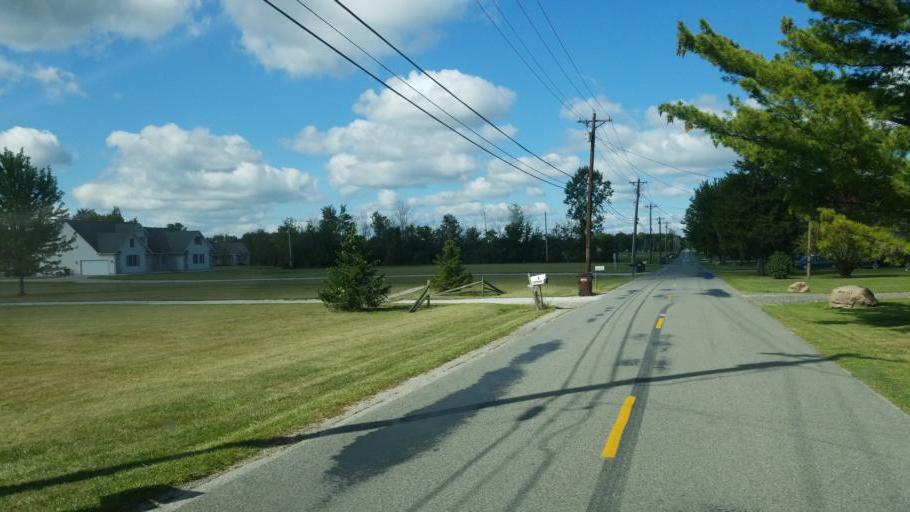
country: US
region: Ohio
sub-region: Lorain County
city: Lagrange
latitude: 41.1998
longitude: -82.1495
